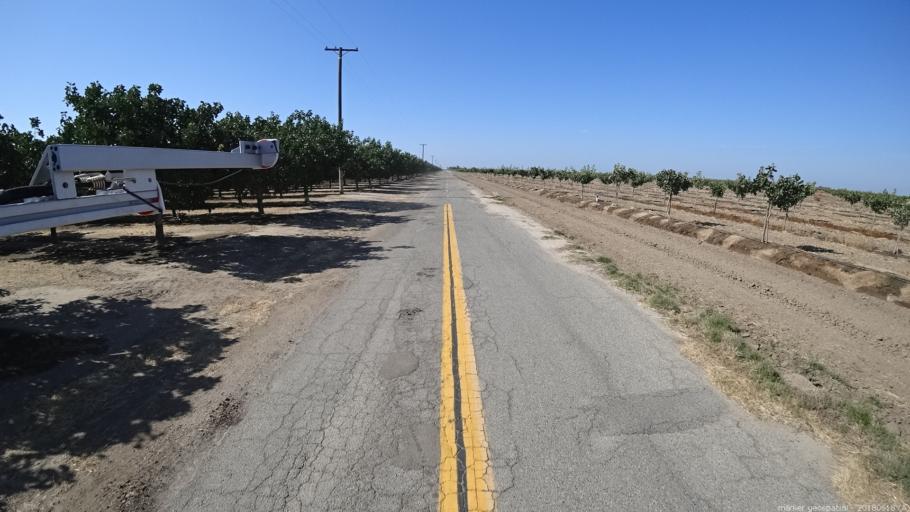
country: US
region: California
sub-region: Madera County
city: Parkwood
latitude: 36.8939
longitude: -120.1558
